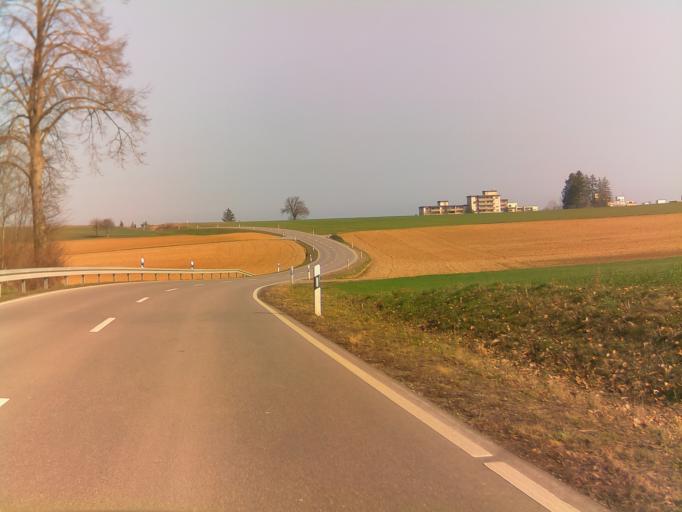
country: DE
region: Baden-Wuerttemberg
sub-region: Regierungsbezirk Stuttgart
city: Eberdingen
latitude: 48.8764
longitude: 9.0002
